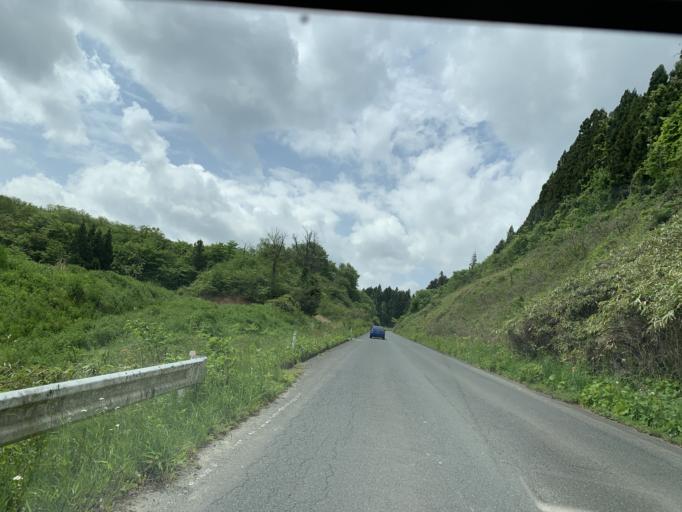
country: JP
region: Miyagi
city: Furukawa
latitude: 38.7224
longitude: 140.9235
